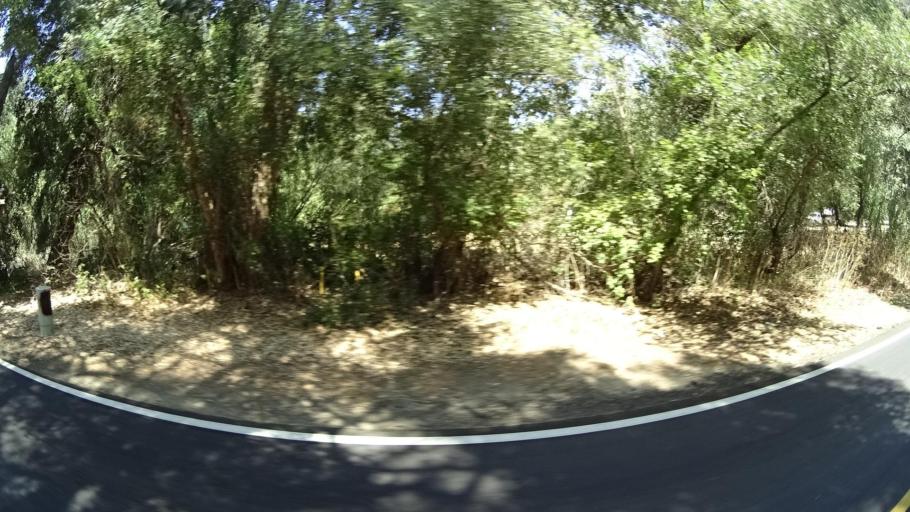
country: US
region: California
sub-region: San Diego County
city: Fallbrook
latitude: 33.4018
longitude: -117.2524
